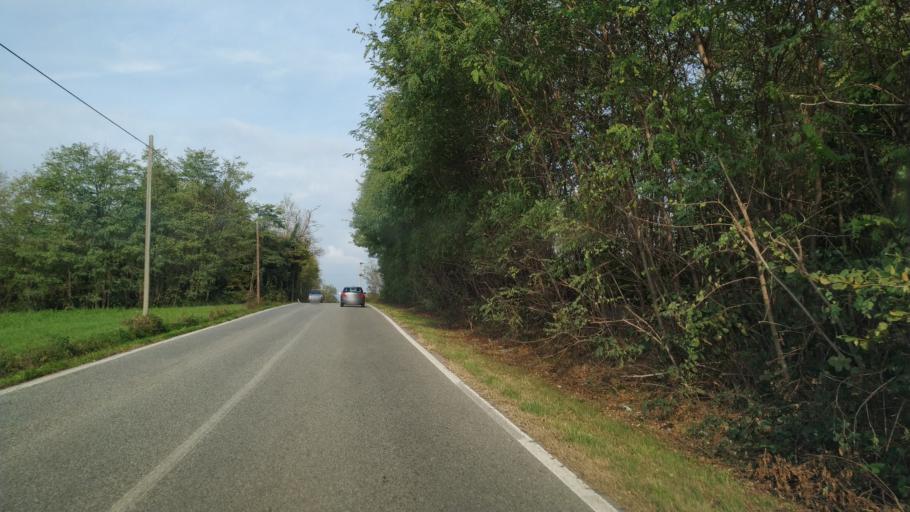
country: IT
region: Piedmont
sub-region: Provincia di Biella
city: Borriana
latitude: 45.5013
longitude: 8.0591
